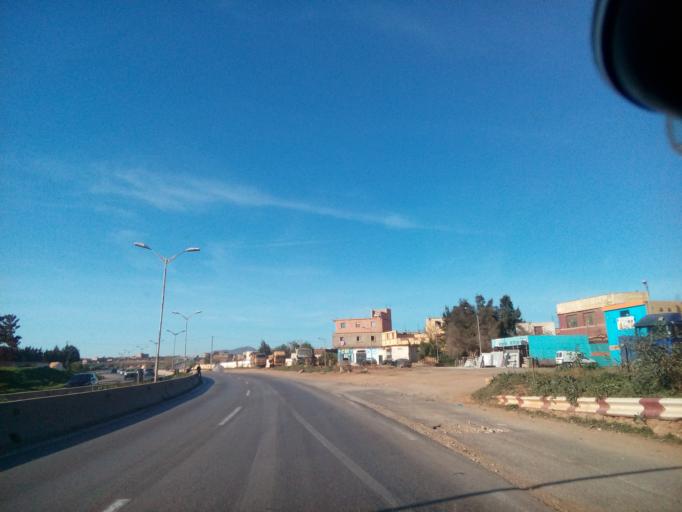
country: DZ
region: Oran
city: Ain el Bya
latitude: 35.7992
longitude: -0.3697
